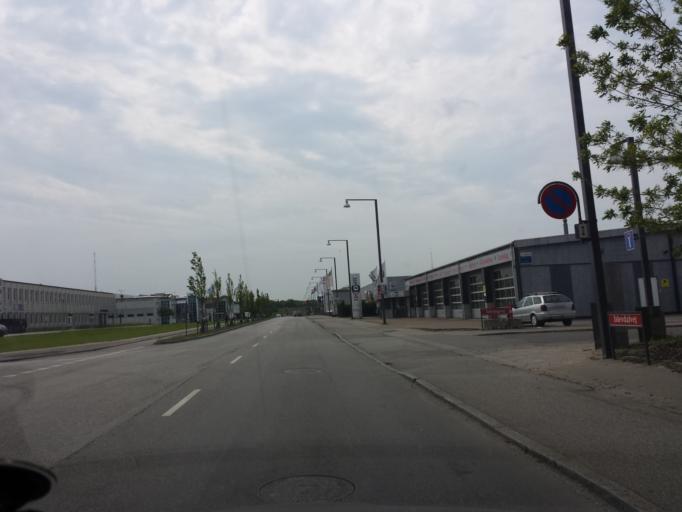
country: DK
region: Capital Region
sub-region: Rodovre Kommune
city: Rodovre
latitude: 55.6956
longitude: 12.4326
